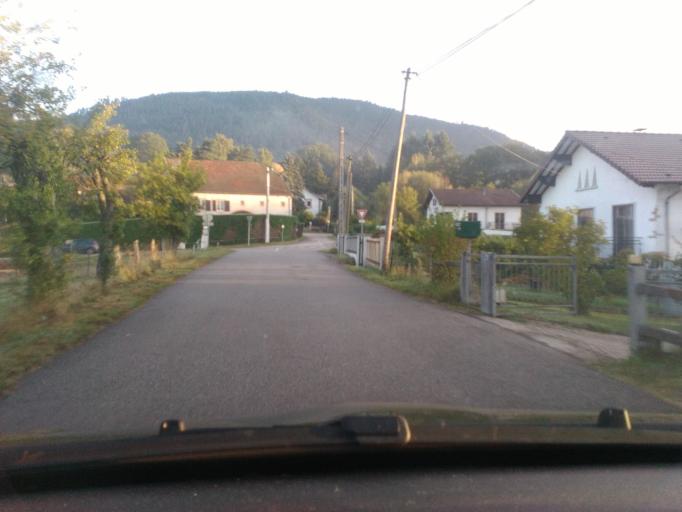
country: FR
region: Lorraine
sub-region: Departement des Vosges
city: Sainte-Marguerite
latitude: 48.2857
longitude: 6.9951
